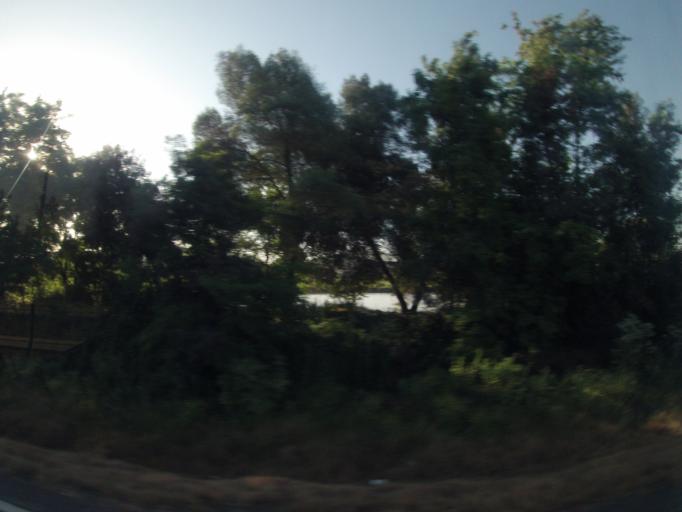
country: CL
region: O'Higgins
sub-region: Provincia de Colchagua
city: Chimbarongo
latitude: -34.6779
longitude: -71.0056
